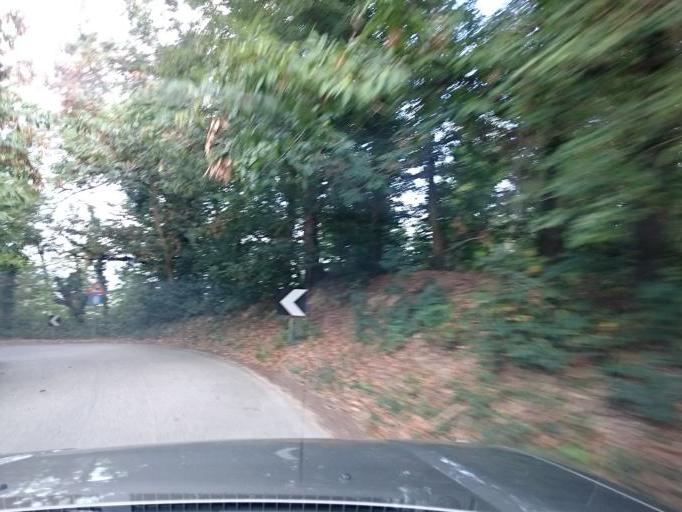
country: IT
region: Veneto
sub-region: Provincia di Padova
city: Galzignano
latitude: 45.3184
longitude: 11.7020
